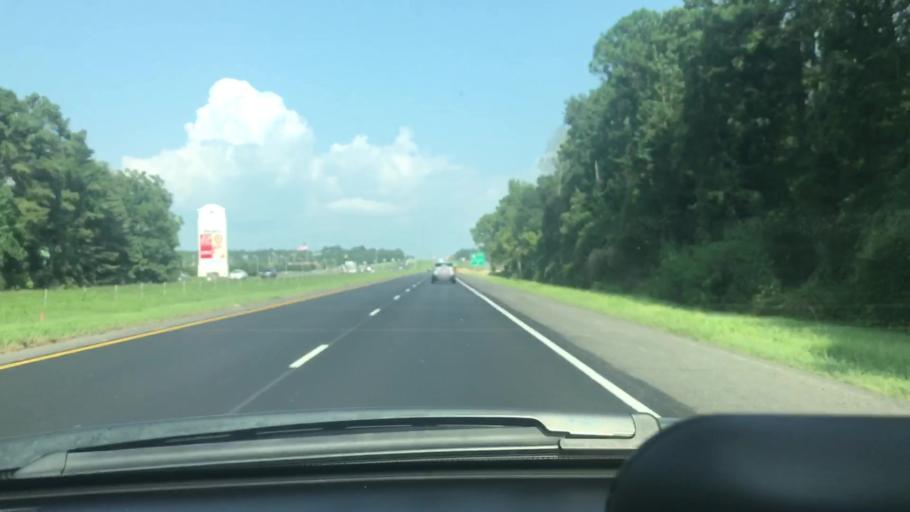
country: US
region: Louisiana
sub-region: Tangipahoa Parish
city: Hammond
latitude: 30.4790
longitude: -90.4656
